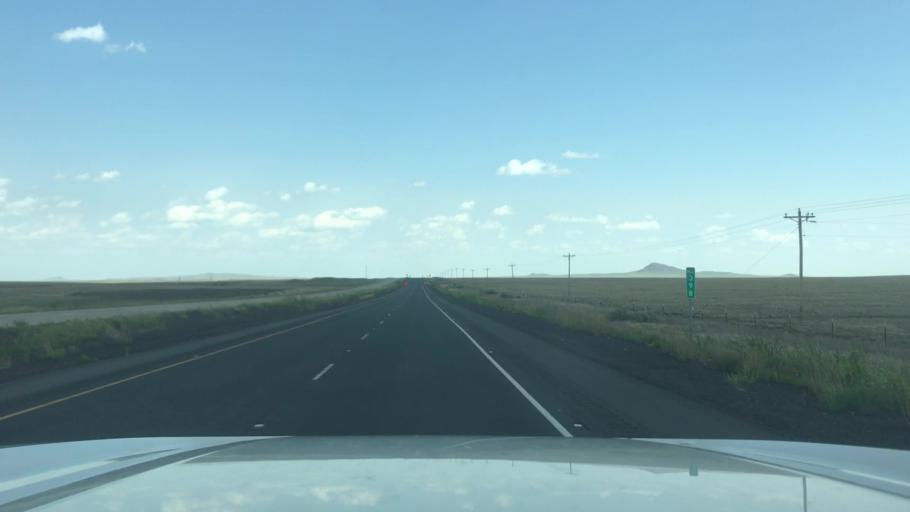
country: US
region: New Mexico
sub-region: Union County
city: Clayton
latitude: 36.6276
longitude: -103.7076
